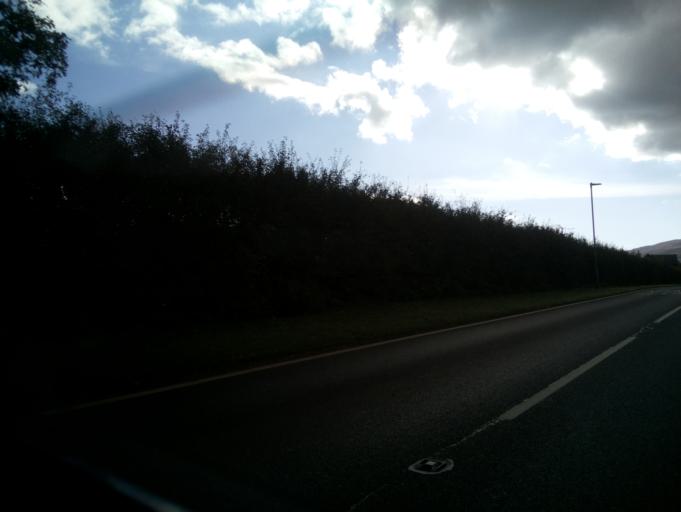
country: GB
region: Wales
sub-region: Sir Powys
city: Brecon
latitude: 51.9254
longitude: -3.4596
